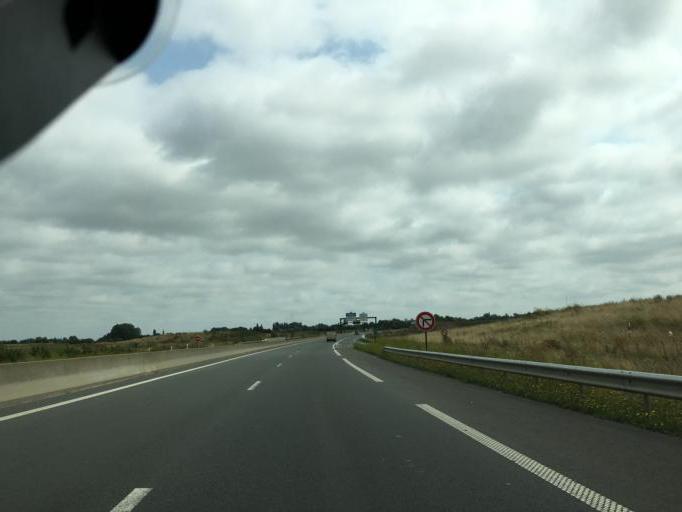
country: FR
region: Nord-Pas-de-Calais
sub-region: Departement du Pas-de-Calais
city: Ranchicourt
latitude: 50.4528
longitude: 2.5676
